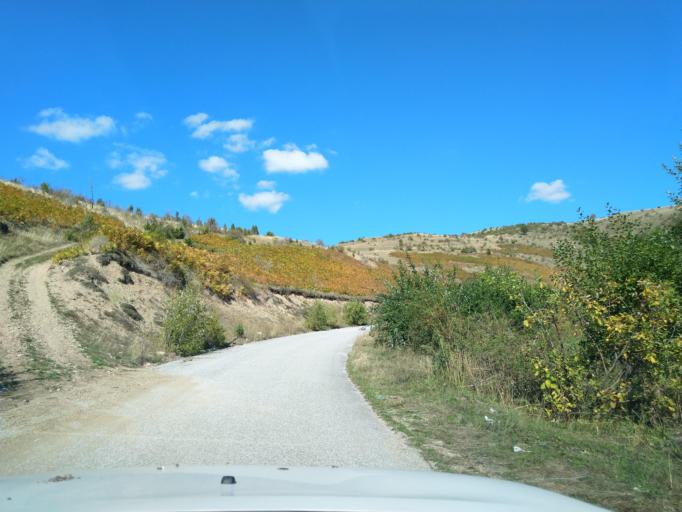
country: RS
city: Sokolovica
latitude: 43.2537
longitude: 20.3325
